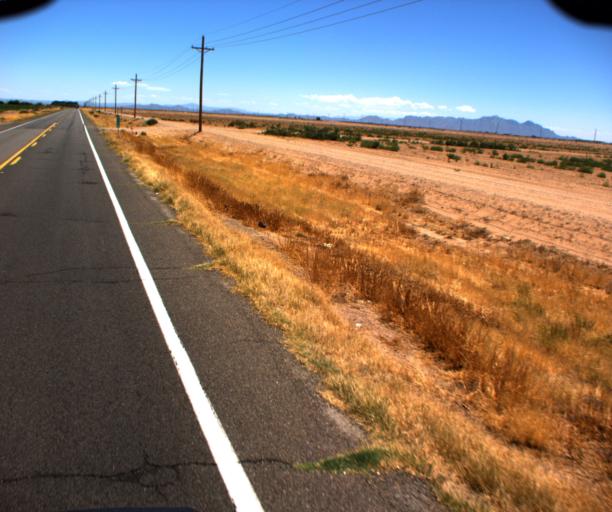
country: US
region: Arizona
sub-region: Pinal County
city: Casa Grande
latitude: 32.8797
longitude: -111.6504
